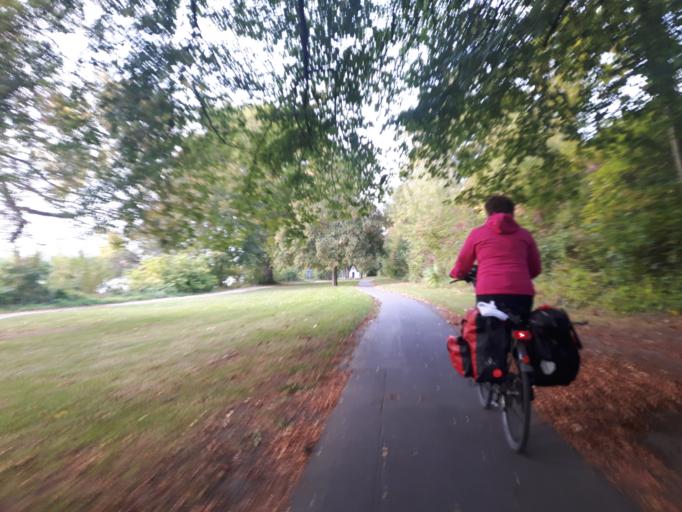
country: DE
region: Rheinland-Pfalz
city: Bad Honningen
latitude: 50.5223
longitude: 7.2994
